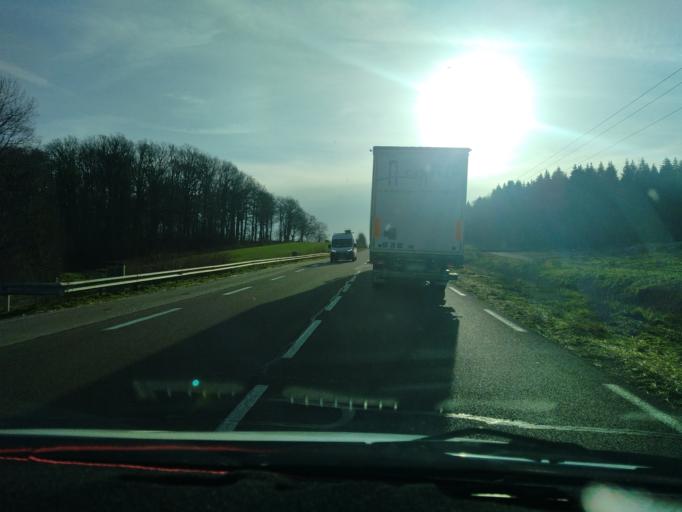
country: FR
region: Franche-Comte
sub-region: Departement de la Haute-Saone
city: Gray
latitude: 47.4184
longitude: 5.6214
